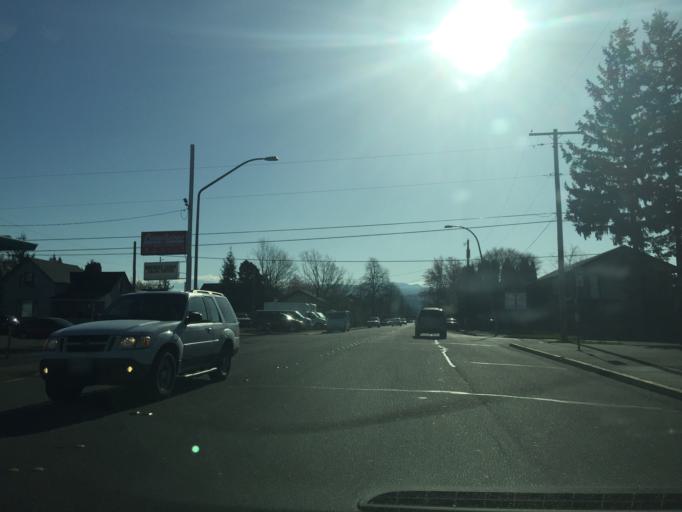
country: US
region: Washington
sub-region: Whatcom County
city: Bellingham
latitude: 48.7610
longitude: -122.4858
